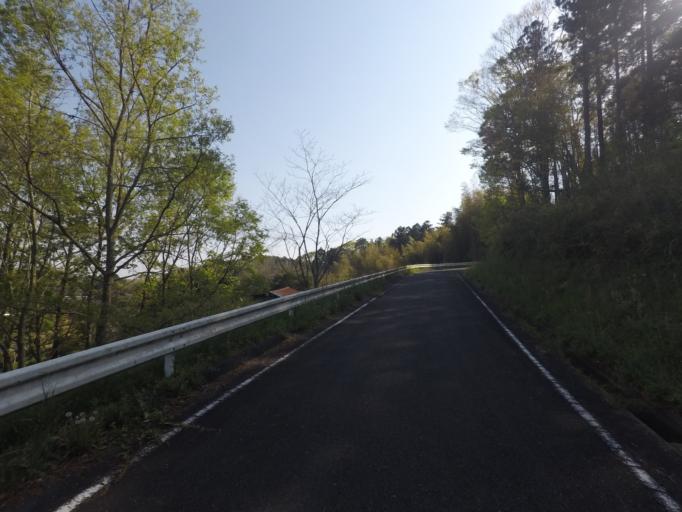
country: JP
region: Ibaraki
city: Itako
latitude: 36.0548
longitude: 140.4493
